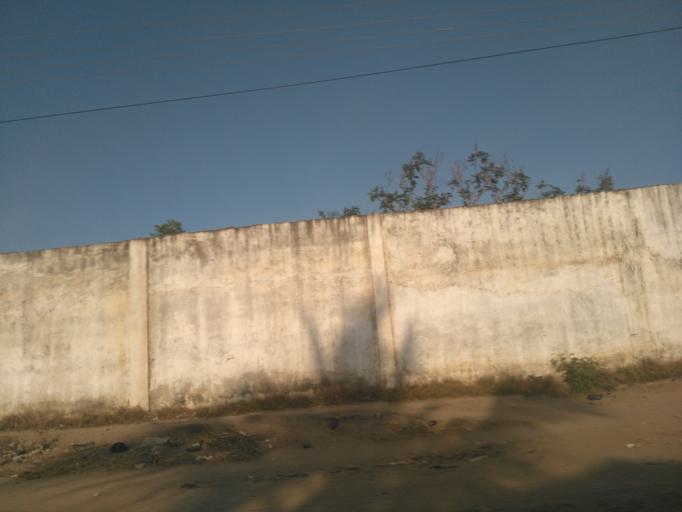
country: TZ
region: Dar es Salaam
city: Dar es Salaam
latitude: -6.9166
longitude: 39.2680
